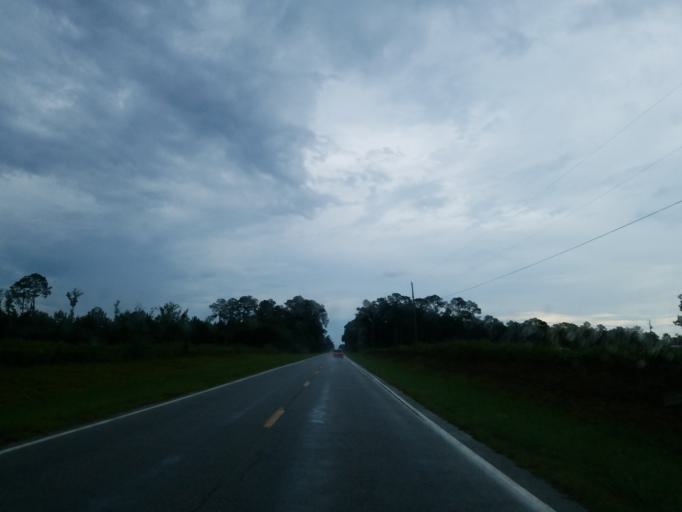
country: US
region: Georgia
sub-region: Berrien County
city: Ray City
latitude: 31.0712
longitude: -83.1803
